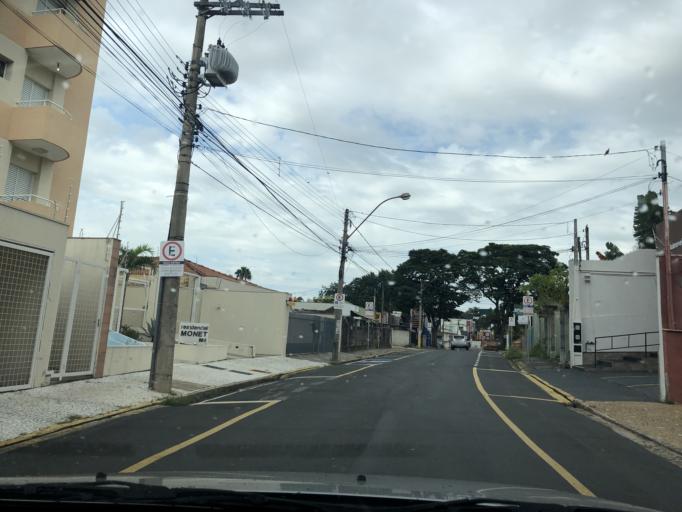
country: BR
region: Sao Paulo
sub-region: Americana
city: Americana
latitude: -22.7421
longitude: -47.3316
